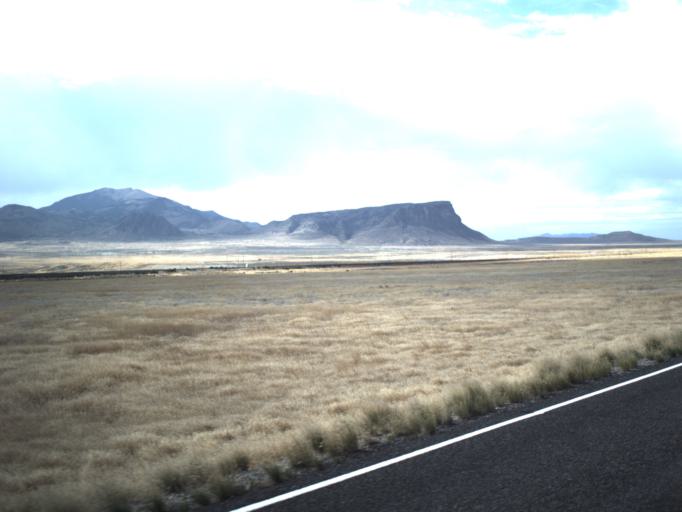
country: US
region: Utah
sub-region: Tooele County
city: Wendover
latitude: 41.3822
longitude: -113.9918
